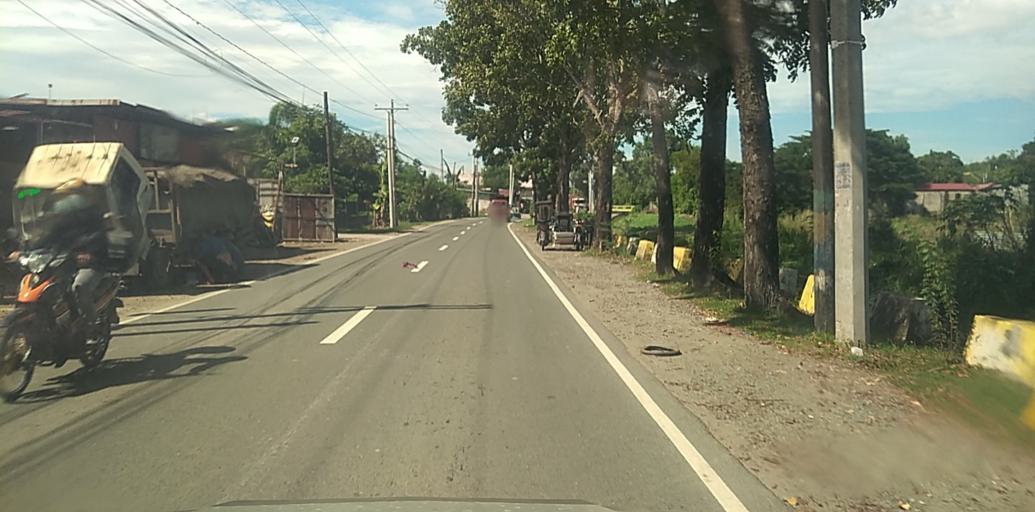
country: PH
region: Central Luzon
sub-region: Province of Pampanga
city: Arayat
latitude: 15.1500
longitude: 120.7492
